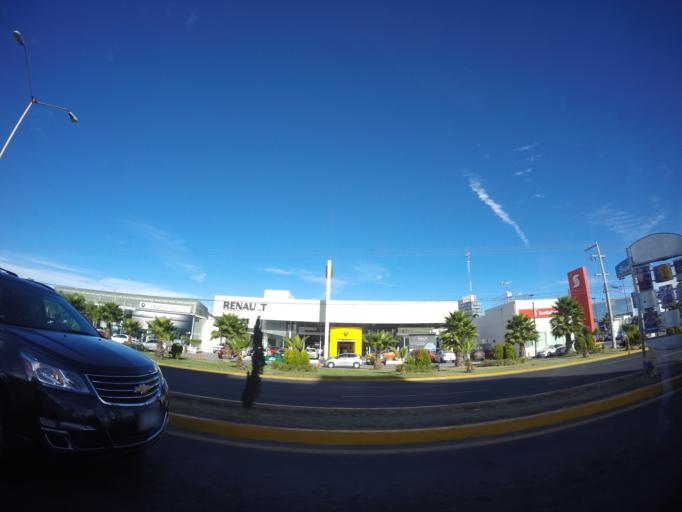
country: MX
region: San Luis Potosi
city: Escalerillas
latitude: 22.1349
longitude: -101.0292
